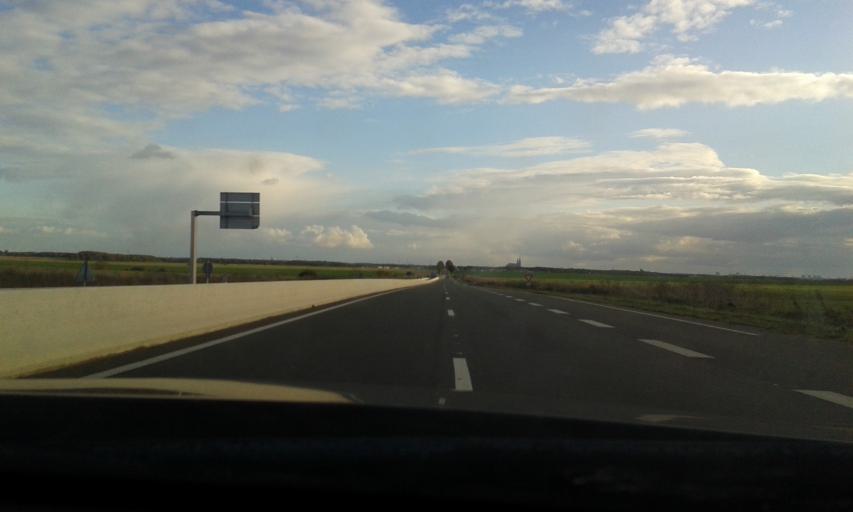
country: FR
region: Centre
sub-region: Departement d'Eure-et-Loir
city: Leves
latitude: 48.5055
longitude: 1.4643
